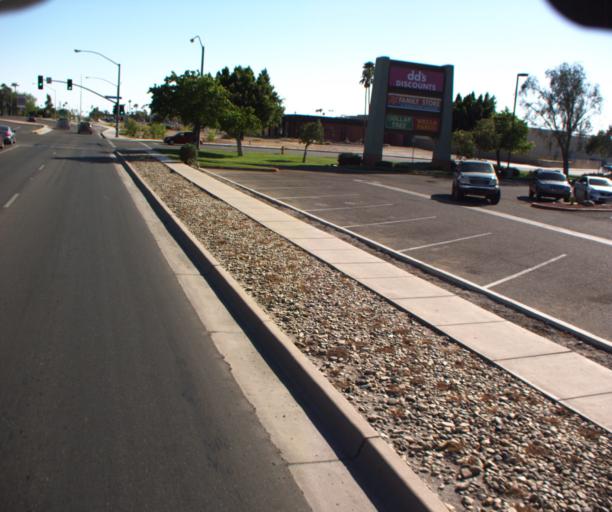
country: US
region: Arizona
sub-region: Yuma County
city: Yuma
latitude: 32.6740
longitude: -114.6246
